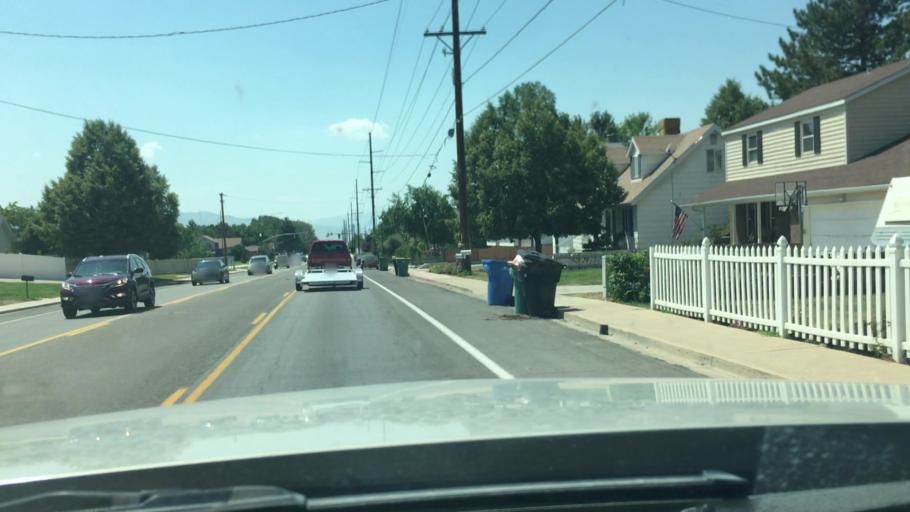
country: US
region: Utah
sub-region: Utah County
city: Lindon
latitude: 40.3265
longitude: -111.7126
